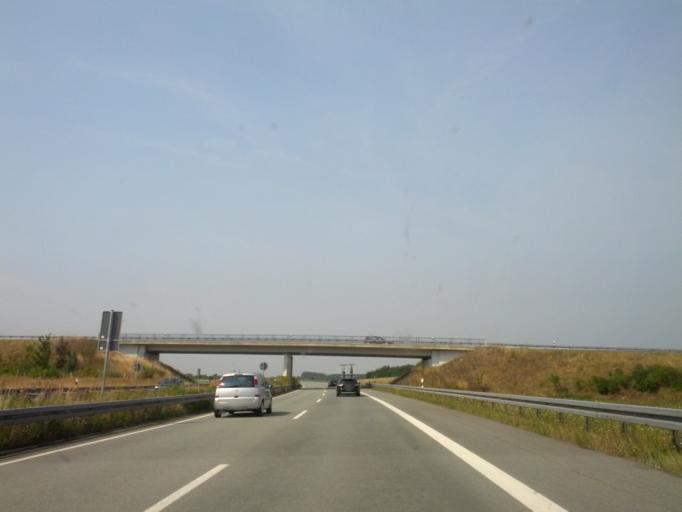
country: DE
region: Mecklenburg-Vorpommern
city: Brandshagen
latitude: 54.2381
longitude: 13.1486
